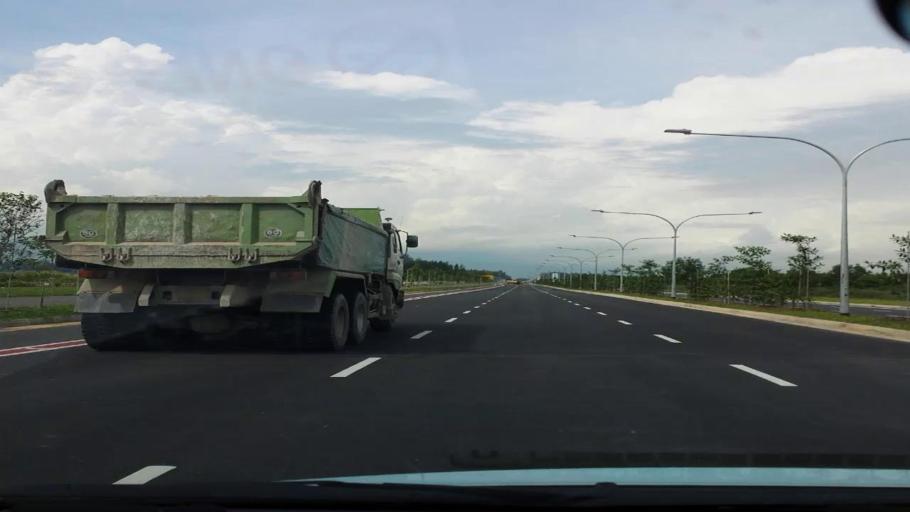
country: SG
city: Singapore
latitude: 1.3434
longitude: 104.0262
